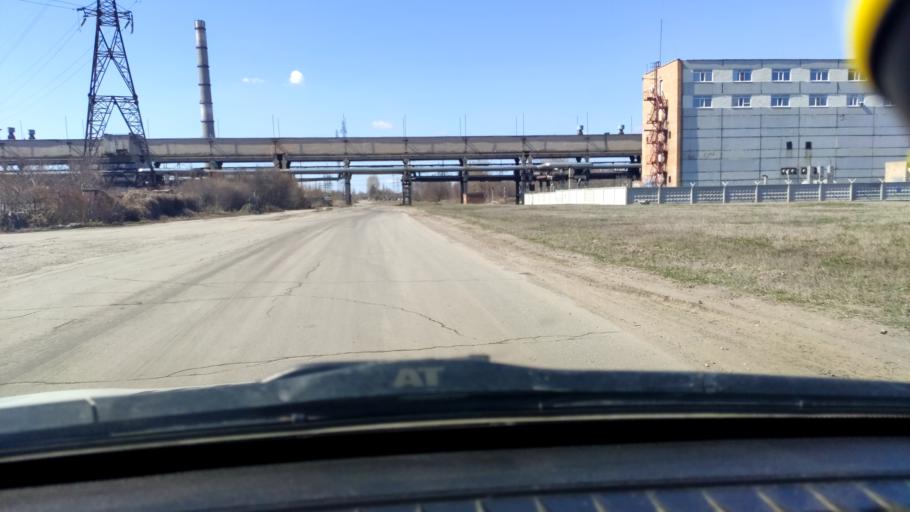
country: RU
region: Samara
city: Tol'yatti
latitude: 53.5494
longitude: 49.4591
